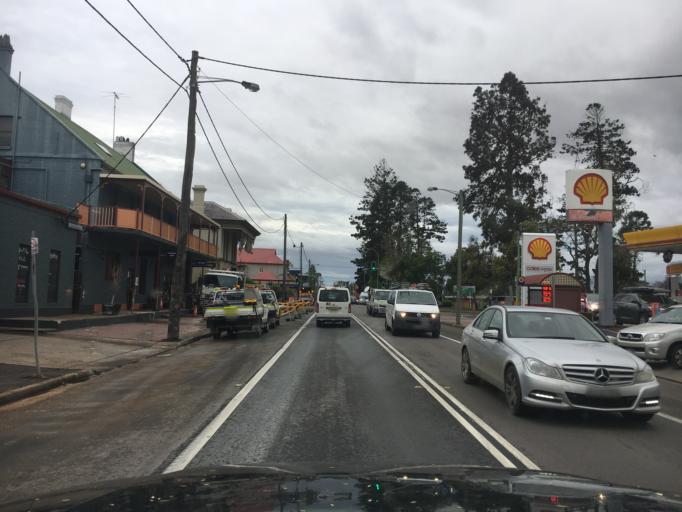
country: AU
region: New South Wales
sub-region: Singleton
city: Singleton
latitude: -32.5626
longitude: 151.1757
